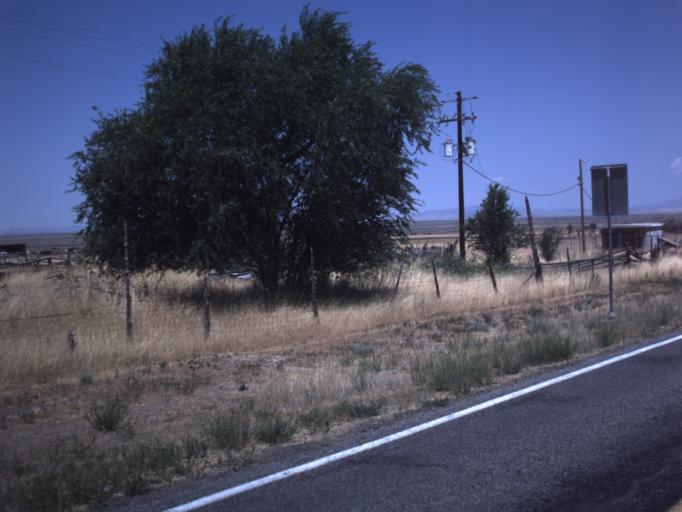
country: US
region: Utah
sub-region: Millard County
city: Delta
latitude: 39.3820
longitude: -112.3360
